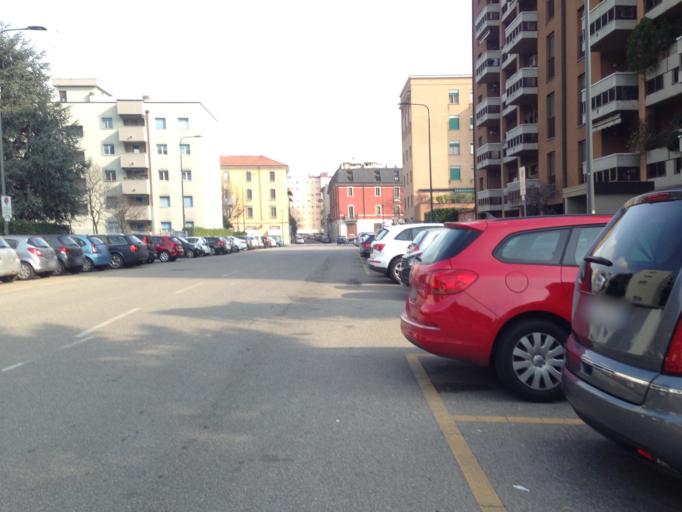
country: IT
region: Lombardy
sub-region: Citta metropolitana di Milano
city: Cesano Boscone
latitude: 45.4714
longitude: 9.1076
